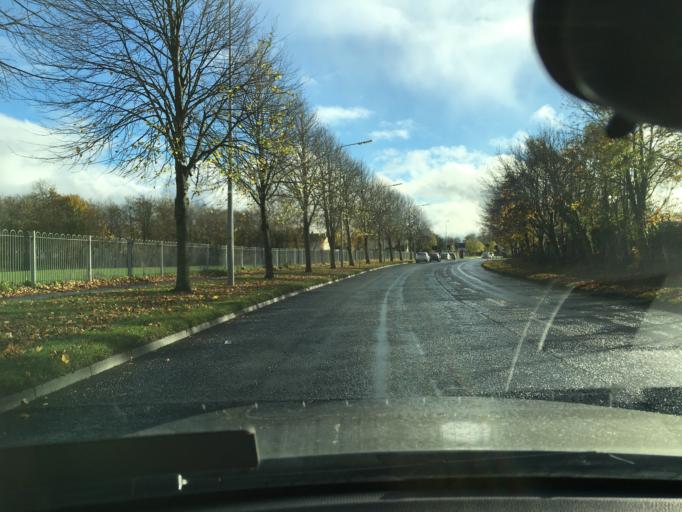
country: IE
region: Leinster
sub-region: Fingal County
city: Blanchardstown
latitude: 53.3844
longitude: -6.3952
